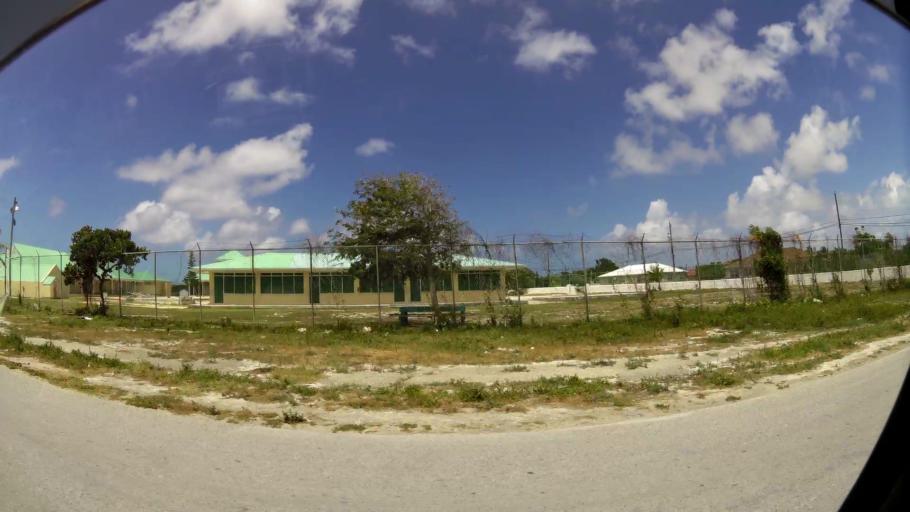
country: TC
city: Cockburn Town
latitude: 21.4570
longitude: -71.1400
